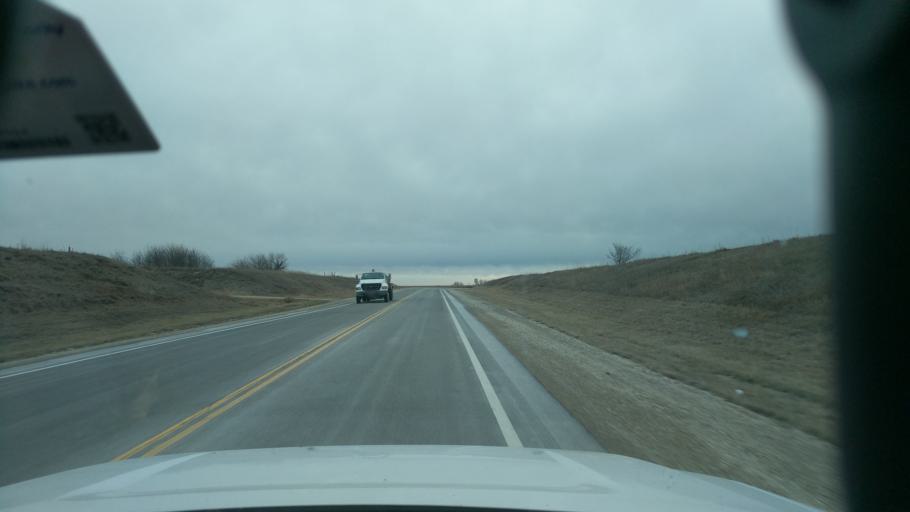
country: US
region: Kansas
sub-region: Marion County
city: Marion
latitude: 38.4343
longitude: -96.9577
